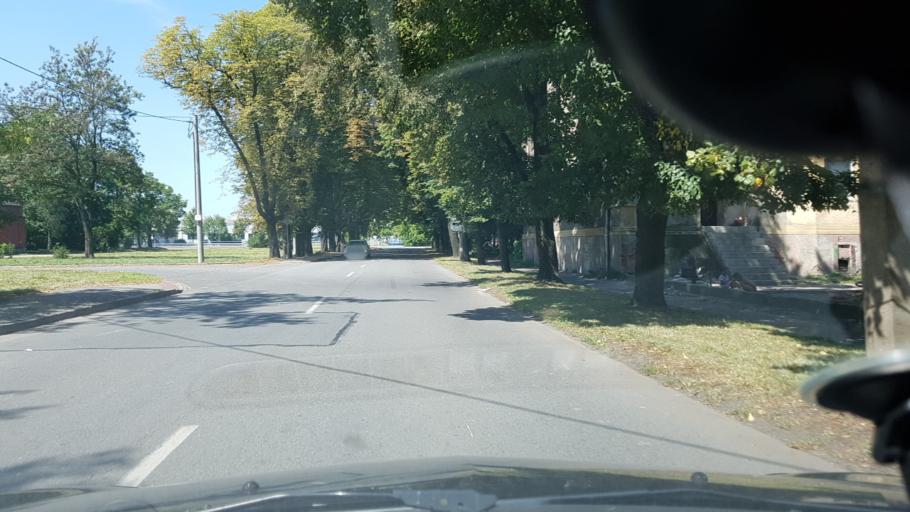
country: CZ
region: Moravskoslezsky
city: Bohumin
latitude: 49.8962
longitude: 18.3463
